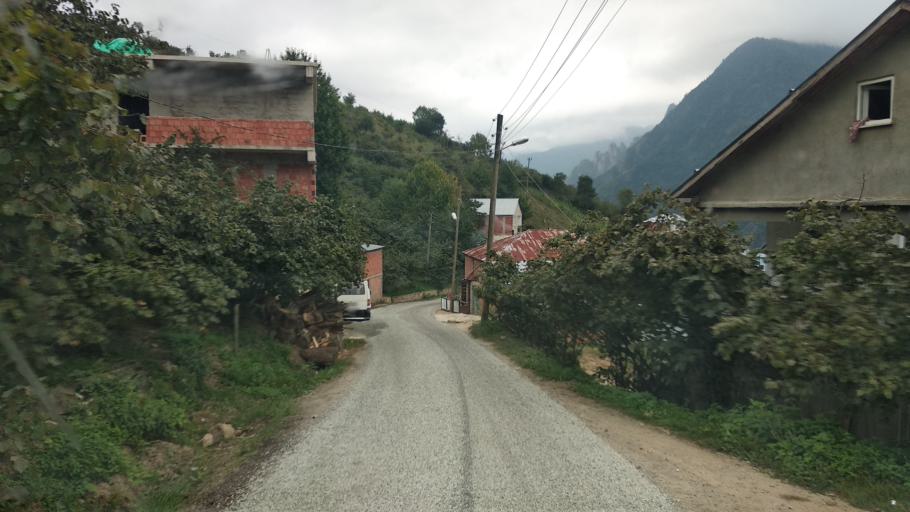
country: TR
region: Giresun
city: Dogankent
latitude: 40.7453
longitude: 38.9903
